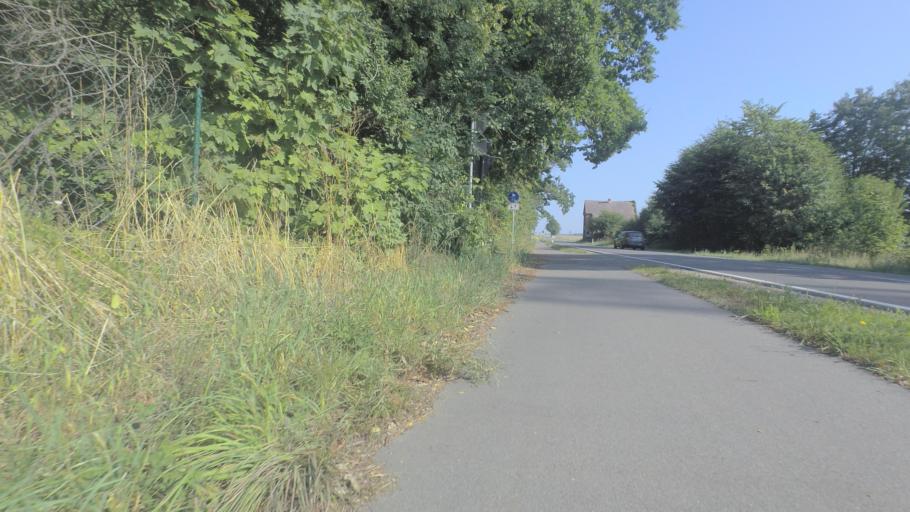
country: DE
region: Mecklenburg-Vorpommern
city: Malchow
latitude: 53.5072
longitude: 12.4225
